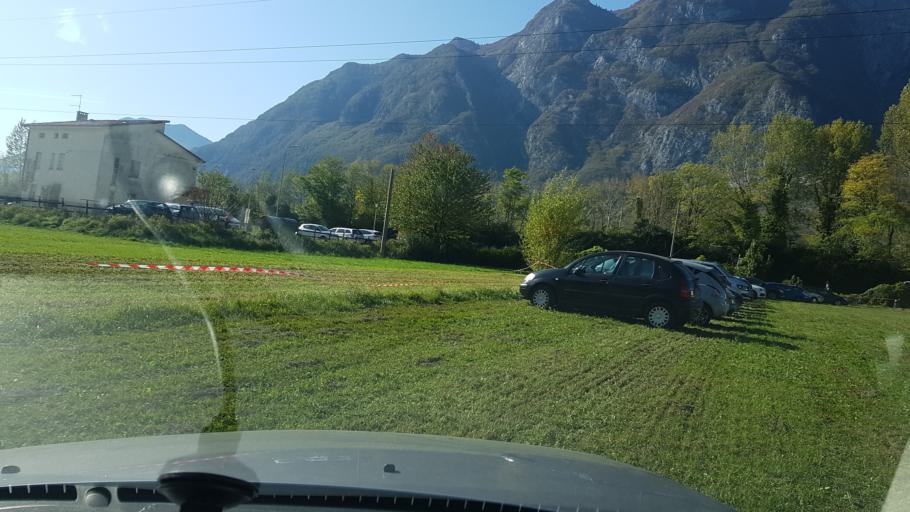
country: IT
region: Friuli Venezia Giulia
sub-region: Provincia di Udine
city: Venzone
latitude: 46.3397
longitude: 13.1408
